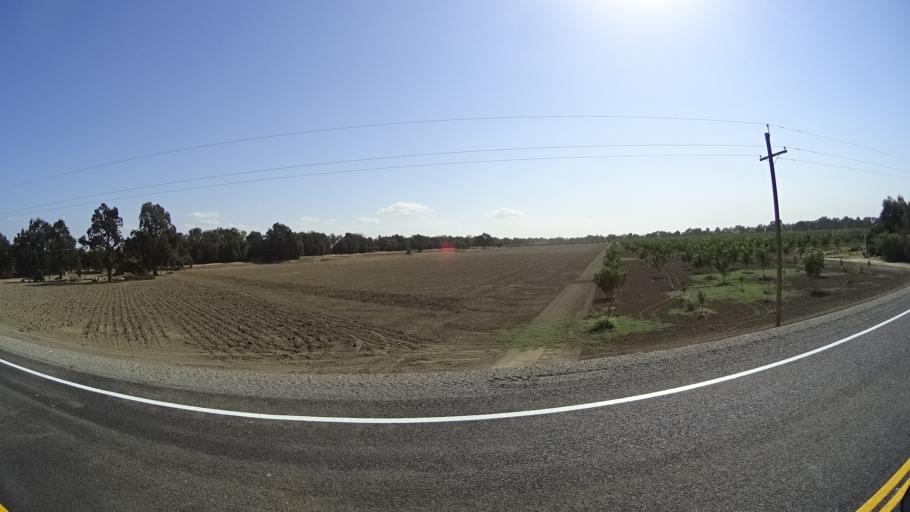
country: US
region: California
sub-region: Yolo County
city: West Sacramento
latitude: 38.6425
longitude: -121.5864
